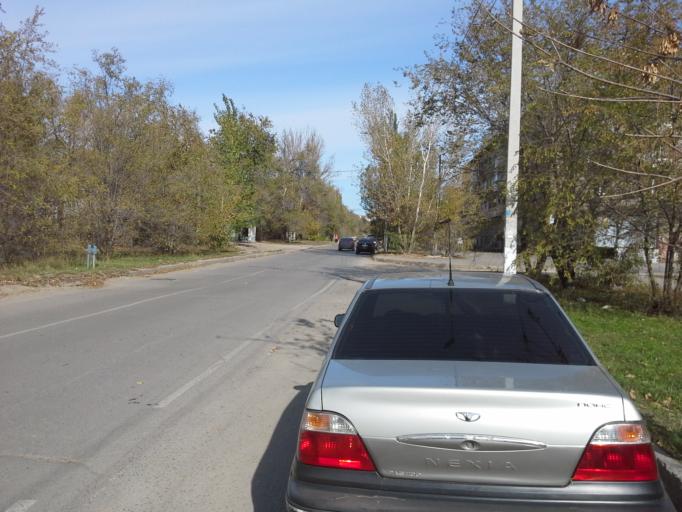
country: RU
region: Volgograd
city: Vodstroy
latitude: 48.8394
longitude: 44.6377
